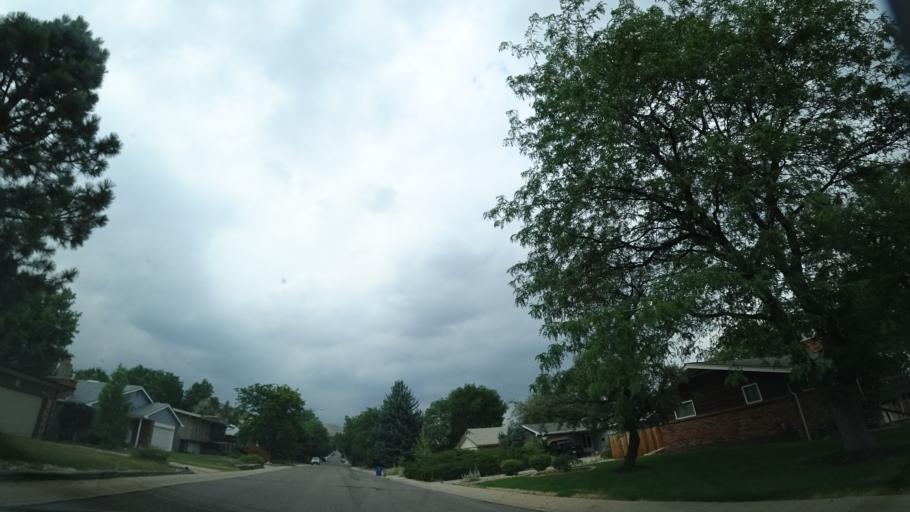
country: US
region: Colorado
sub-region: Jefferson County
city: West Pleasant View
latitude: 39.7087
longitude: -105.1479
